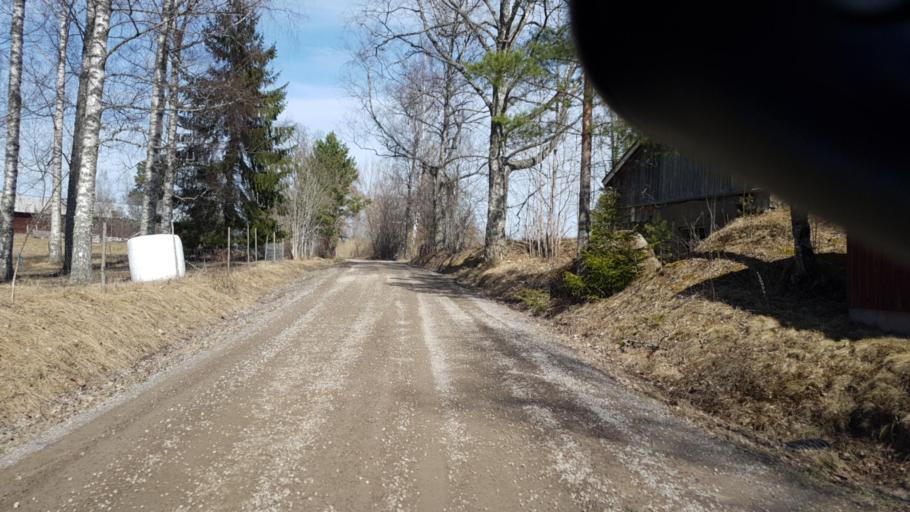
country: SE
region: Vaermland
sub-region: Grums Kommun
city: Grums
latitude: 59.4845
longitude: 12.9343
